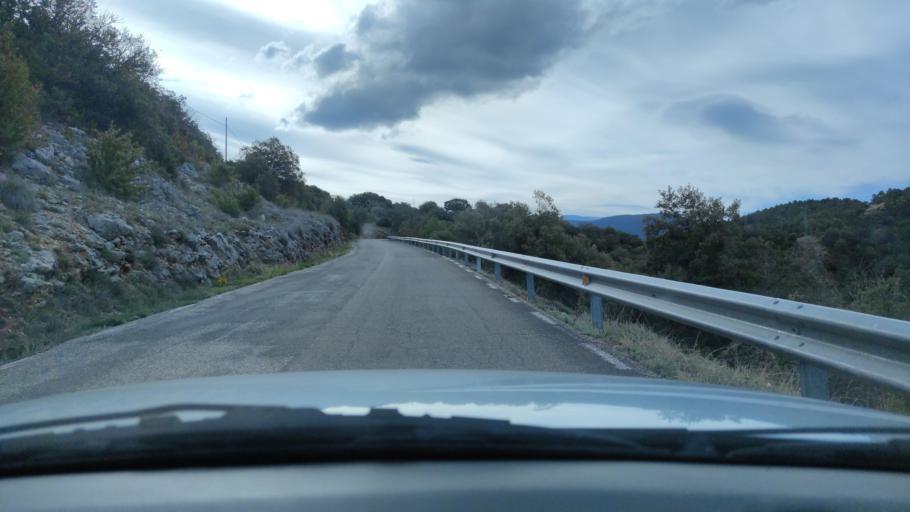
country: ES
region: Catalonia
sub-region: Provincia de Lleida
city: Coll de Nargo
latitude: 42.2404
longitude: 1.3706
